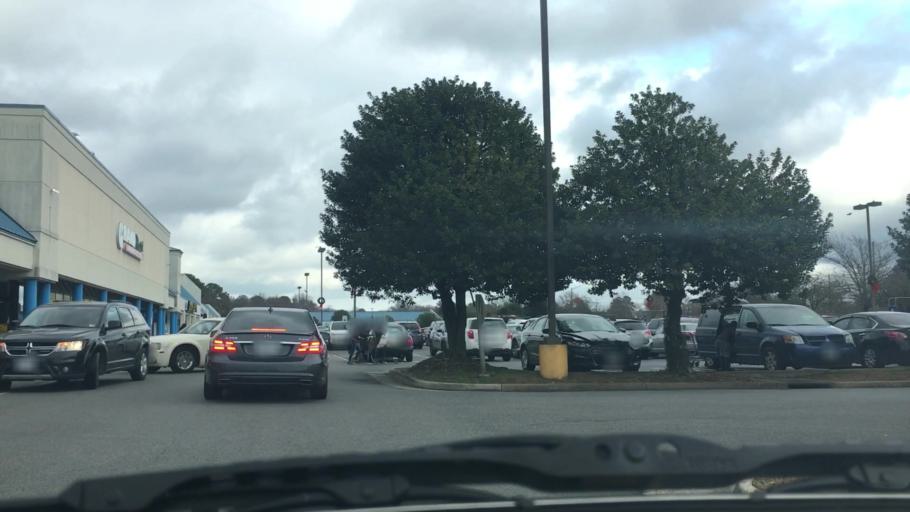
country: US
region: Virginia
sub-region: City of Chesapeake
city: Chesapeake
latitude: 36.8614
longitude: -76.1746
